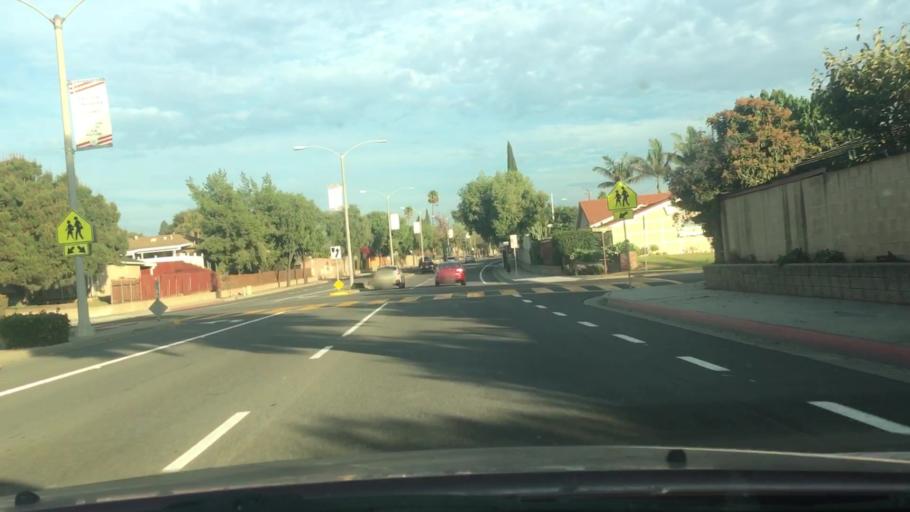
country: US
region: California
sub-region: Los Angeles County
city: La Mirada
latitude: 33.8990
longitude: -118.0016
